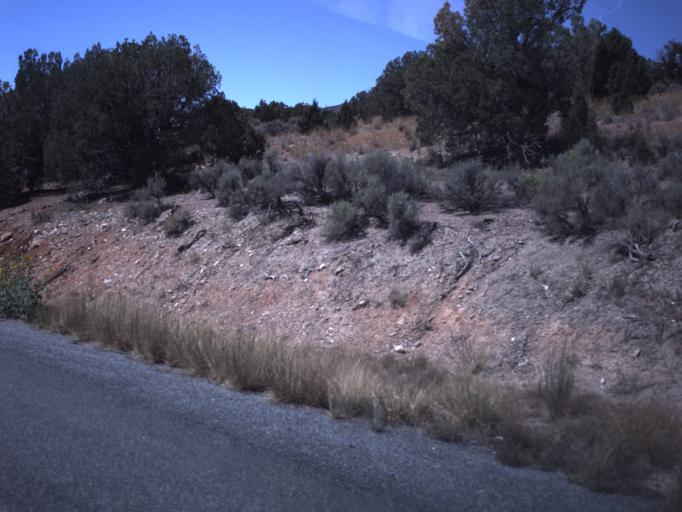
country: US
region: Utah
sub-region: Juab County
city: Nephi
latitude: 39.5919
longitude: -112.1567
